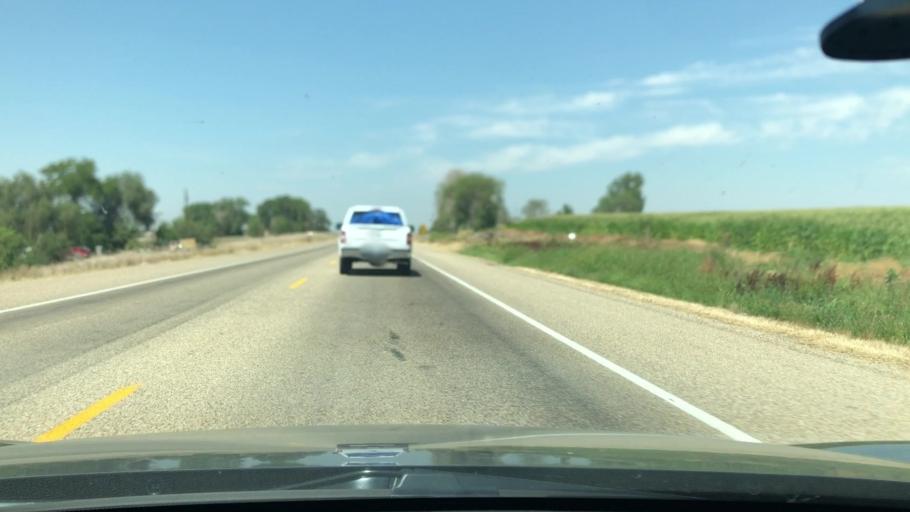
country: US
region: Idaho
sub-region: Canyon County
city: Parma
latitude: 43.8330
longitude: -116.9545
